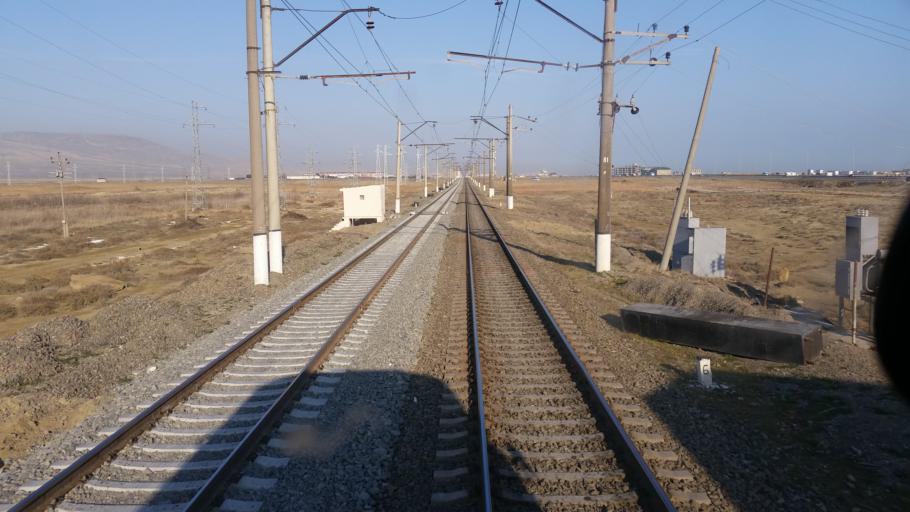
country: AZ
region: Baki
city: Qobustan
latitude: 40.1865
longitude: 49.4885
